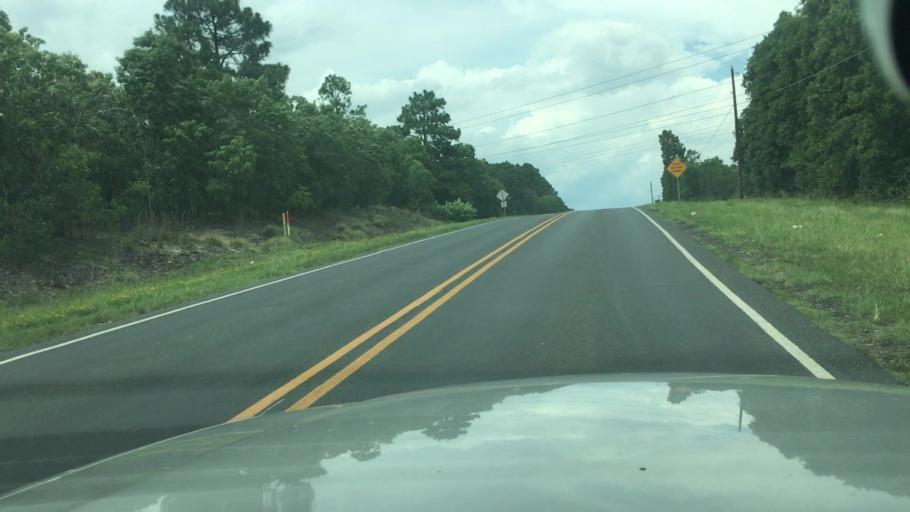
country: US
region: North Carolina
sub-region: Cumberland County
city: Hope Mills
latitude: 34.9655
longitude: -78.8930
